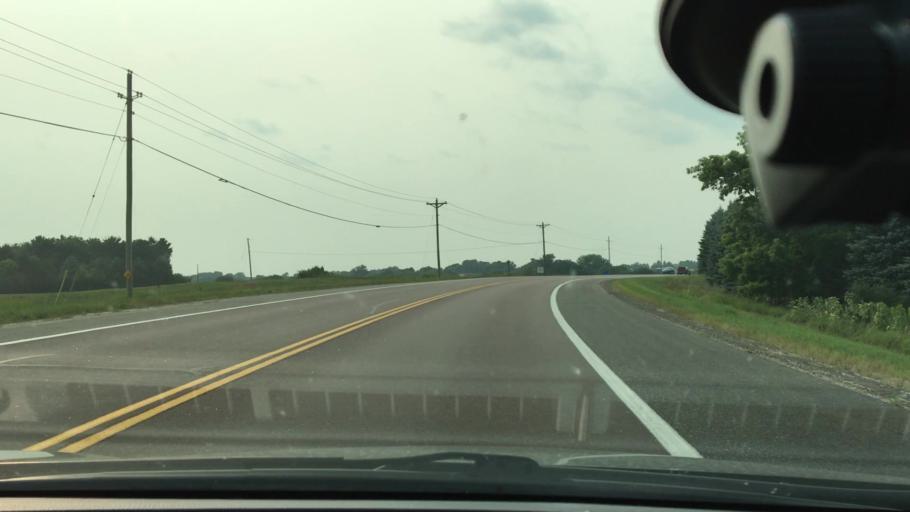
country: US
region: Minnesota
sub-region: Hennepin County
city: Dayton
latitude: 45.2450
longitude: -93.5293
